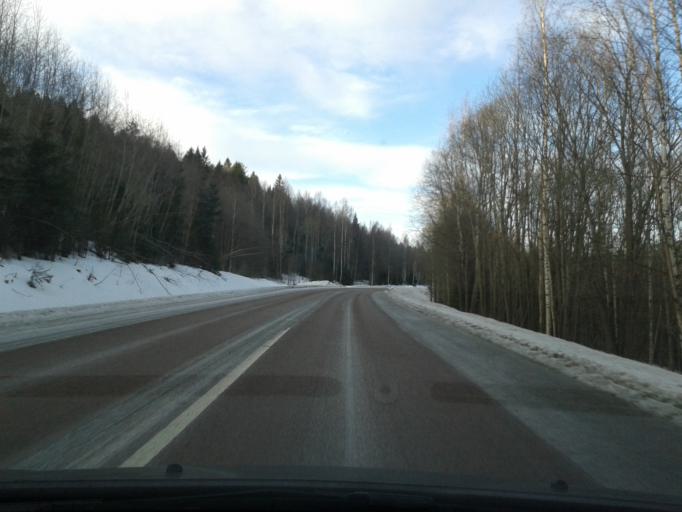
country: SE
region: Vaesternorrland
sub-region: OErnskoeldsviks Kommun
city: Bjasta
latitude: 63.3425
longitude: 18.5042
